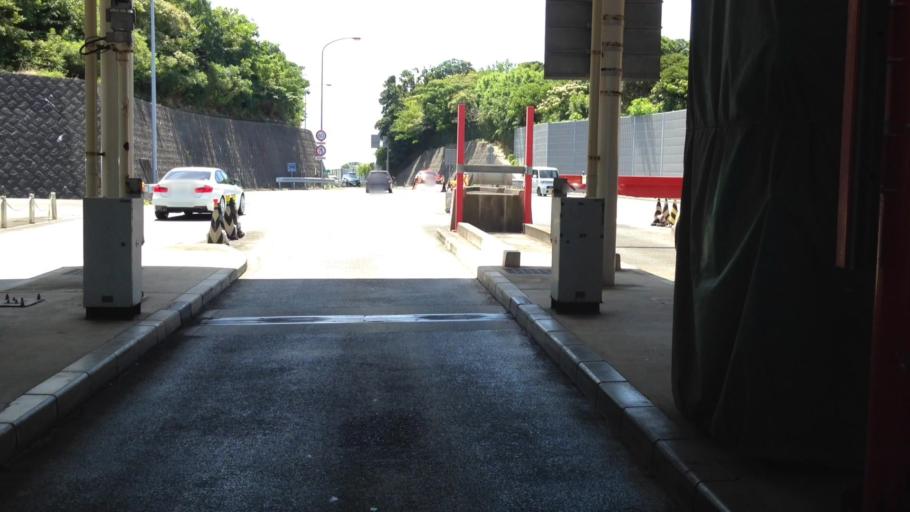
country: JP
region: Kanagawa
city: Yokosuka
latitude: 35.2262
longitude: 139.6387
